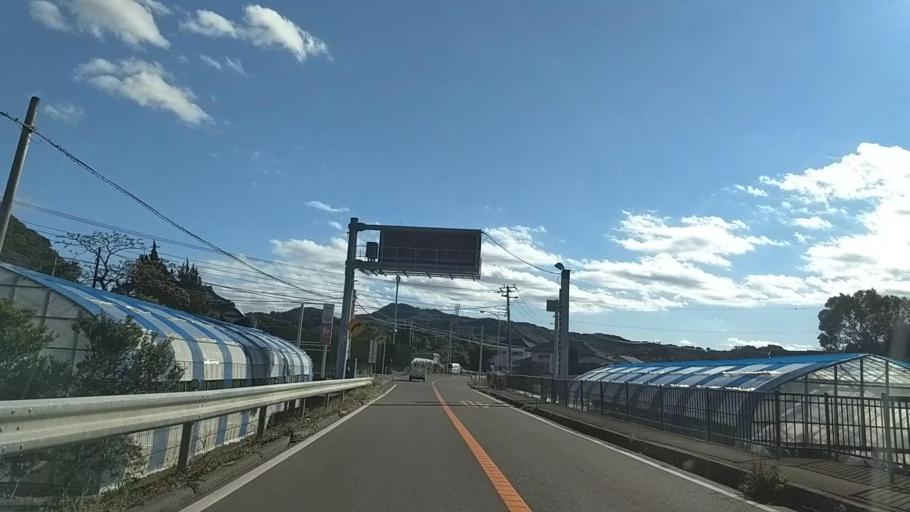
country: JP
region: Chiba
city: Tateyama
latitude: 35.0642
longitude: 139.8254
